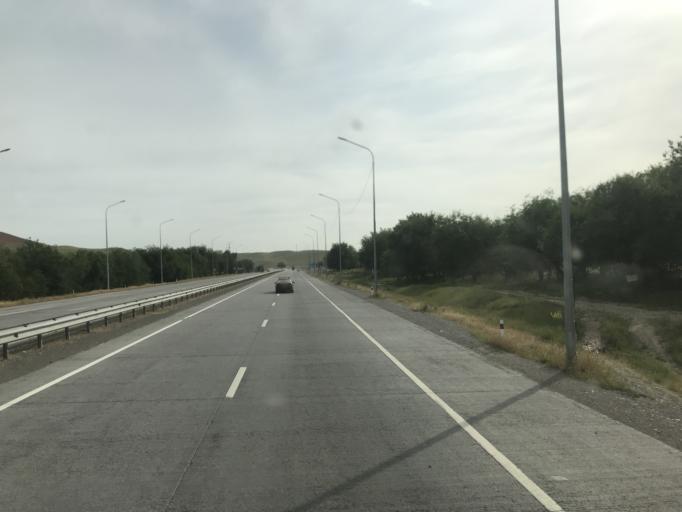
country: KZ
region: Ongtustik Qazaqstan
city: Shymkent
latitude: 42.2157
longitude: 69.5253
